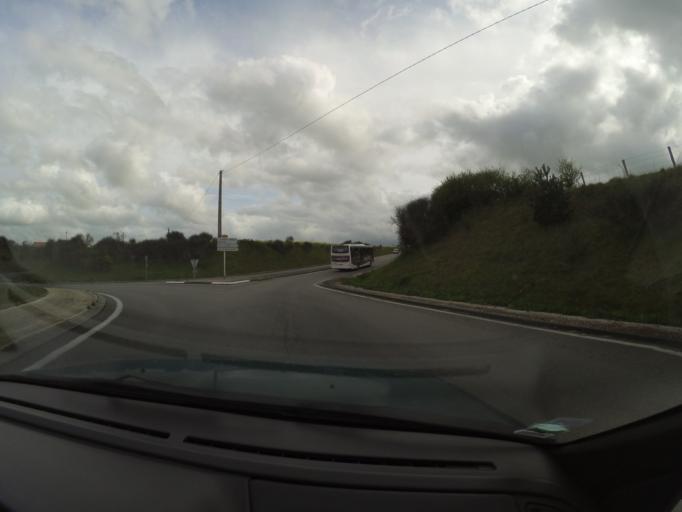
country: FR
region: Pays de la Loire
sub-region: Departement de Maine-et-Loire
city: Lire
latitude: 47.3303
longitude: -1.1678
